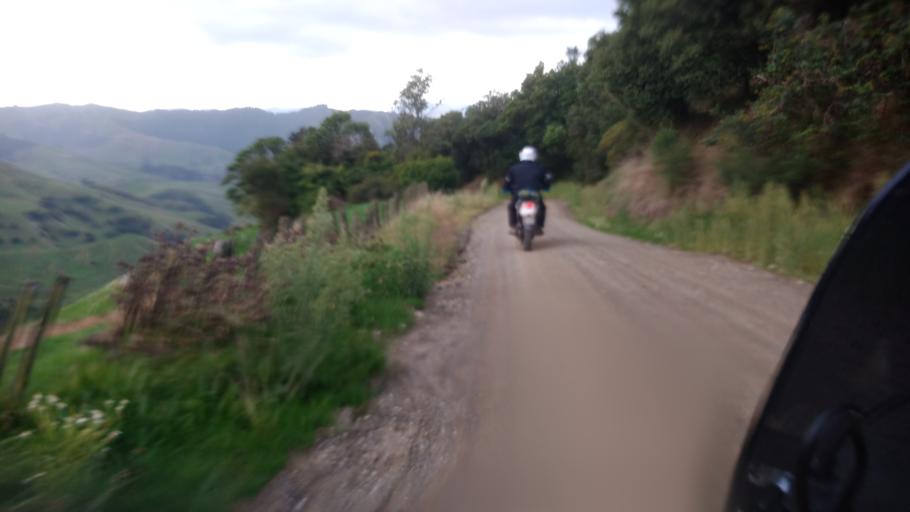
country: NZ
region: Gisborne
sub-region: Gisborne District
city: Gisborne
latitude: -38.4694
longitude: 177.6195
